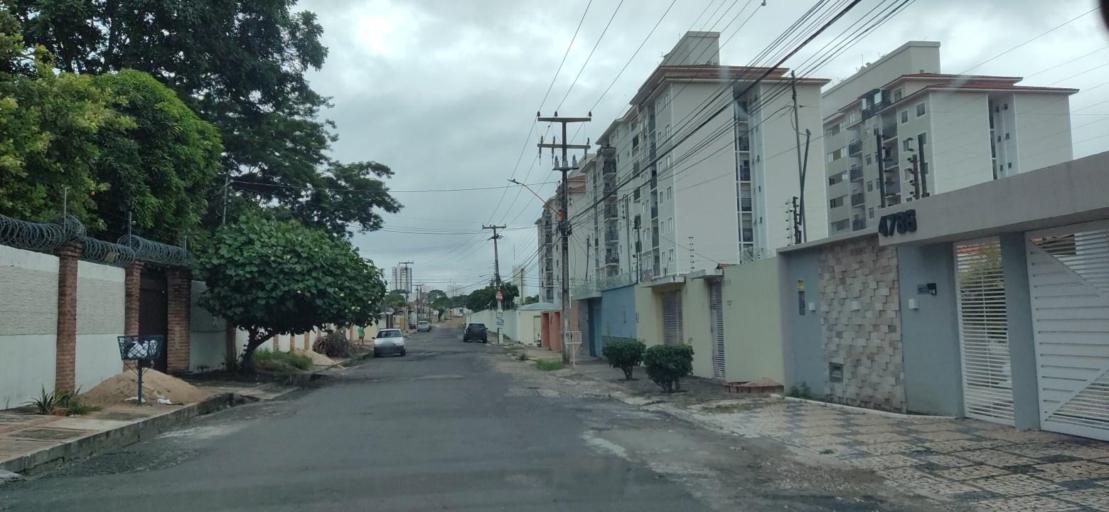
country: BR
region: Piaui
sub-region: Teresina
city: Teresina
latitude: -5.0719
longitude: -42.7582
